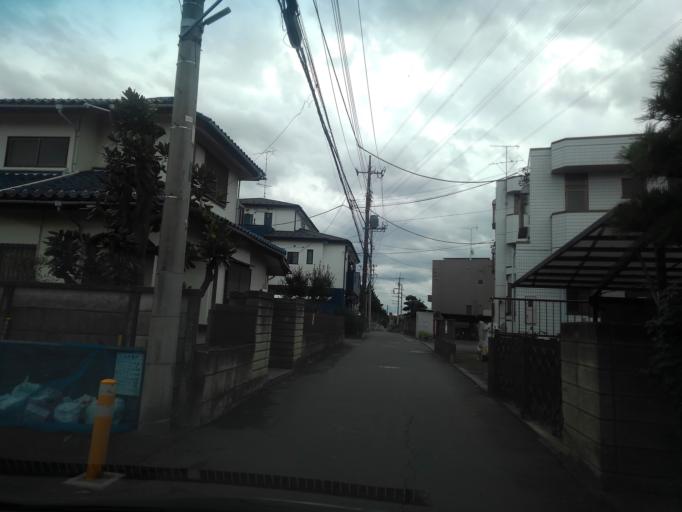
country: JP
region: Saitama
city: Tokorozawa
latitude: 35.7888
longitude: 139.4475
